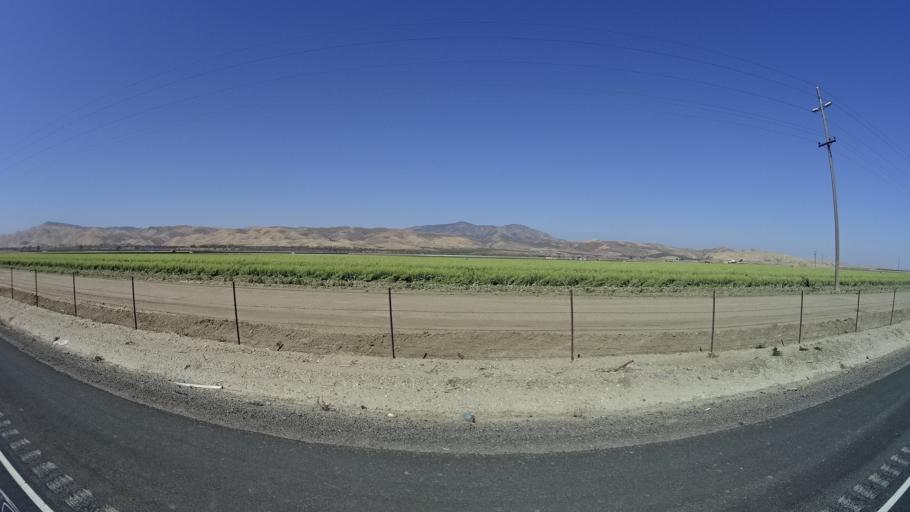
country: US
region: California
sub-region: Monterey County
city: Soledad
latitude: 36.3934
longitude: -121.3094
